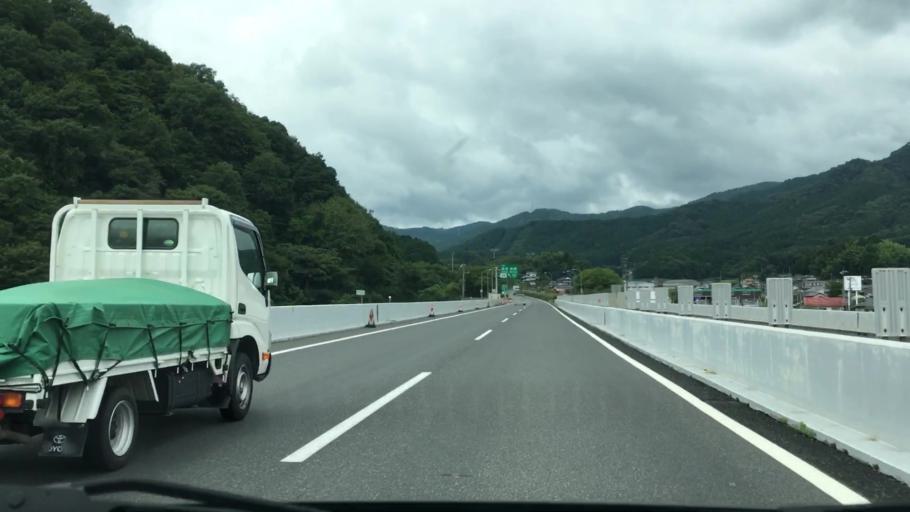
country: JP
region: Okayama
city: Tsuyama
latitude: 35.0245
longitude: 133.7521
